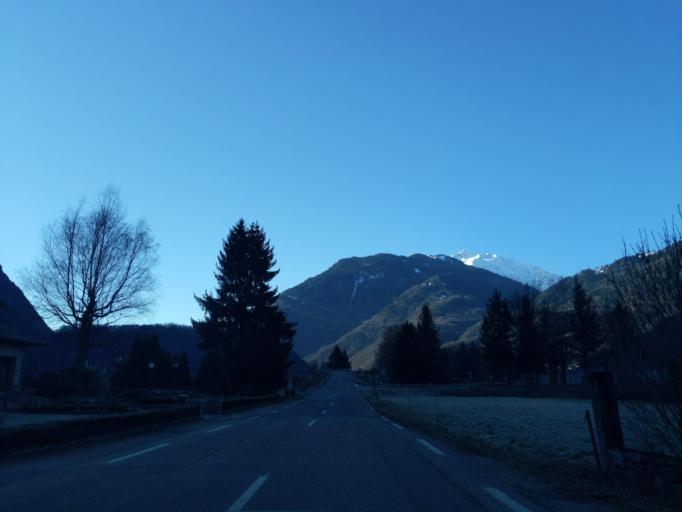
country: FR
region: Rhone-Alpes
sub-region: Departement de la Savoie
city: La Bathie
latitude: 45.6114
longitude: 6.4522
